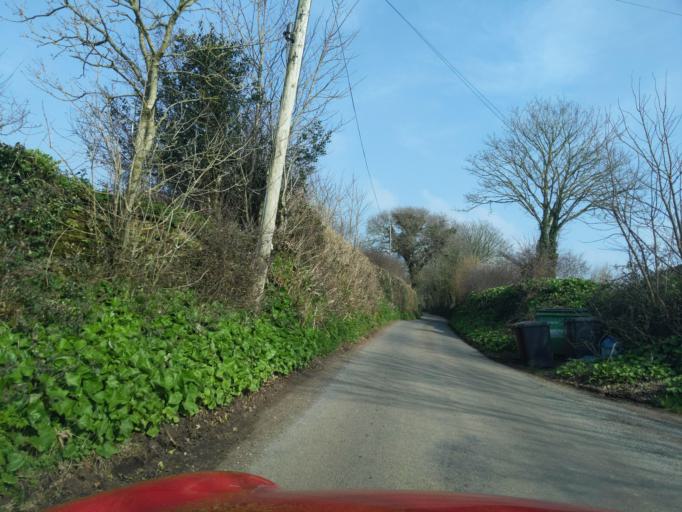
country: GB
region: England
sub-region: Devon
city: Kingsbridge
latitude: 50.2918
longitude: -3.7419
